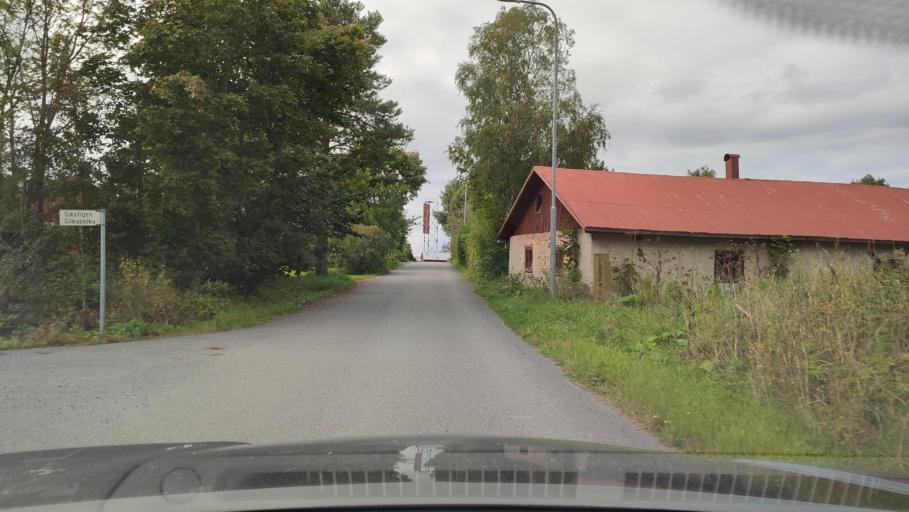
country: FI
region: Ostrobothnia
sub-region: Sydosterbotten
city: Kristinestad
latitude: 62.2779
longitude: 21.3449
